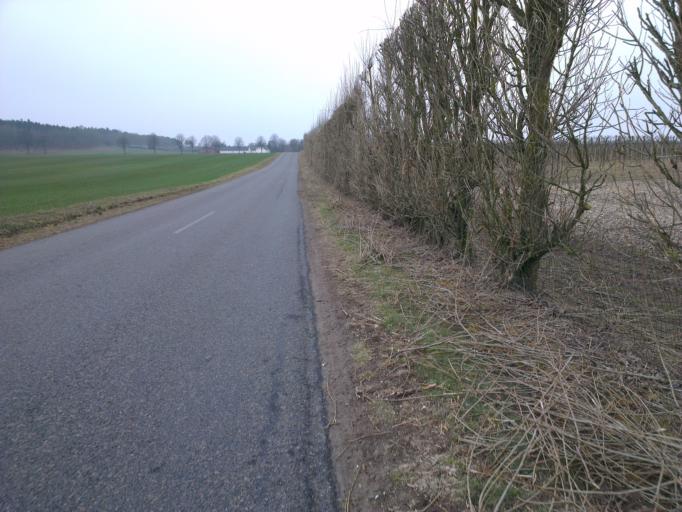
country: DK
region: Capital Region
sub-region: Frederikssund Kommune
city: Skibby
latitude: 55.7923
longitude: 11.9682
